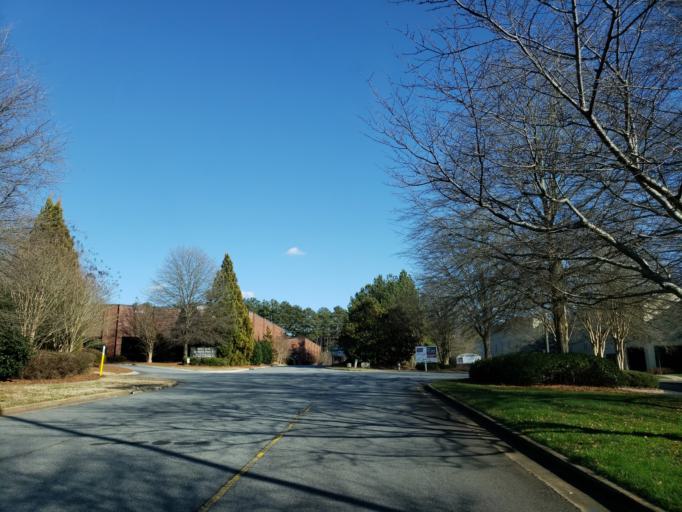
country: US
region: Georgia
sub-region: Cobb County
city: Marietta
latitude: 33.9857
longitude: -84.5169
